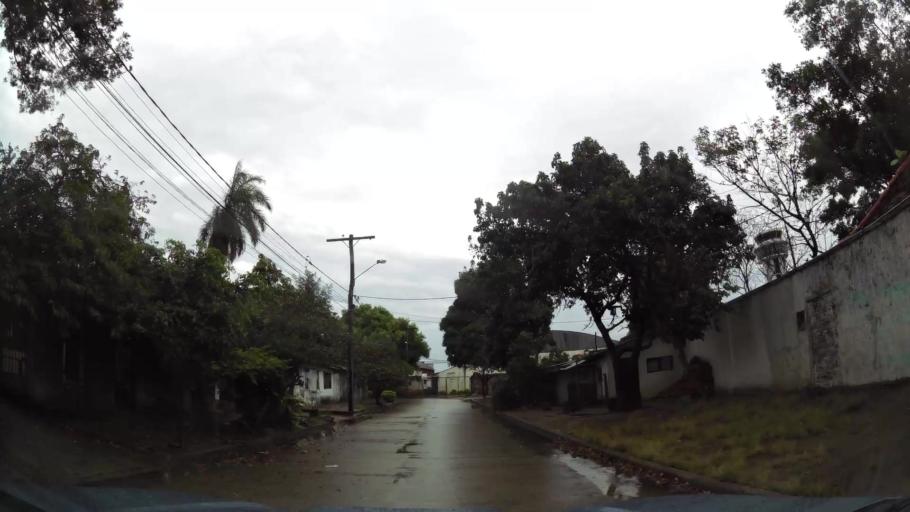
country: BO
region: Santa Cruz
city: Santa Cruz de la Sierra
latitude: -17.8029
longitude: -63.1747
